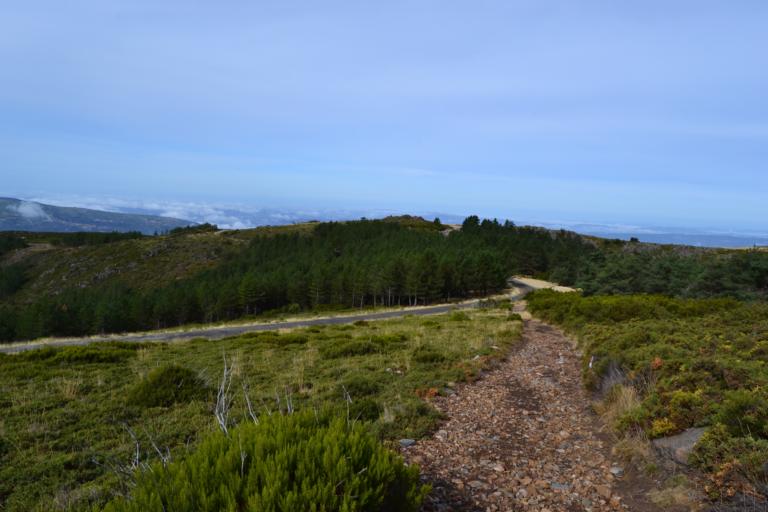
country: PT
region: Vila Real
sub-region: Mesao Frio
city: Mesao Frio
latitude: 41.2480
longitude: -7.8909
